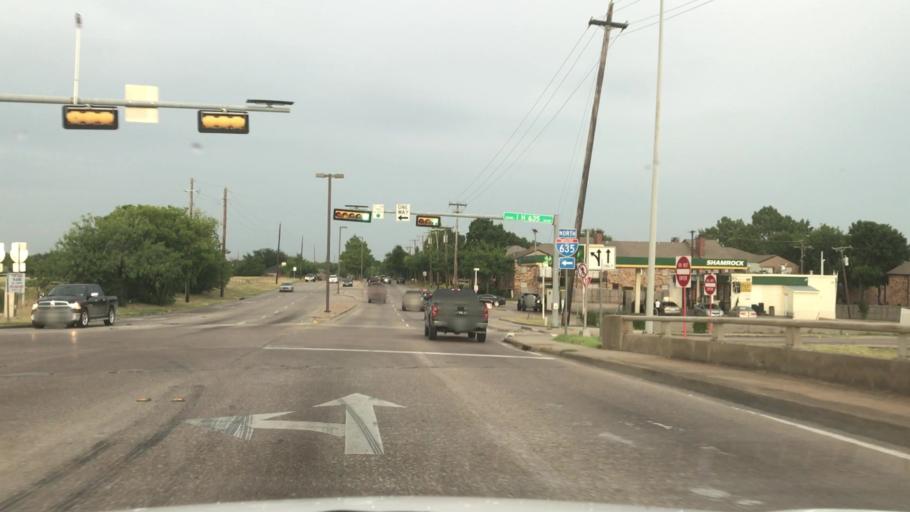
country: US
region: Texas
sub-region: Dallas County
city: Balch Springs
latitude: 32.7485
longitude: -96.6135
